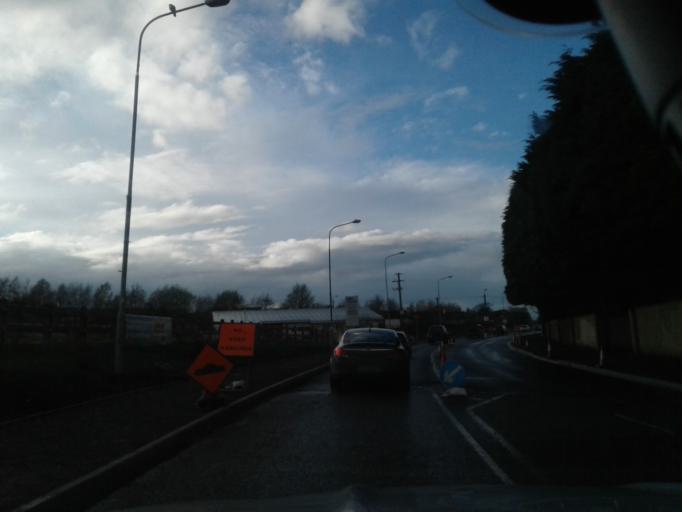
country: IE
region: Ulster
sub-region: County Donegal
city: Leifear
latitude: 54.8342
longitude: -7.4876
